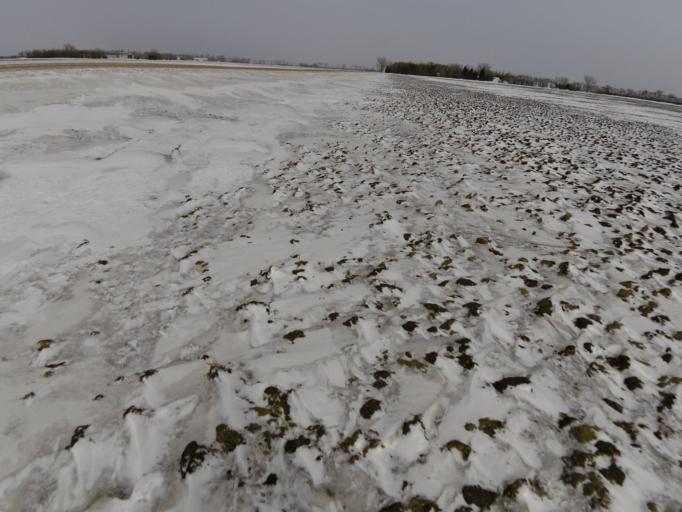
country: US
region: North Dakota
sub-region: Walsh County
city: Grafton
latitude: 48.3995
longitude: -97.2117
